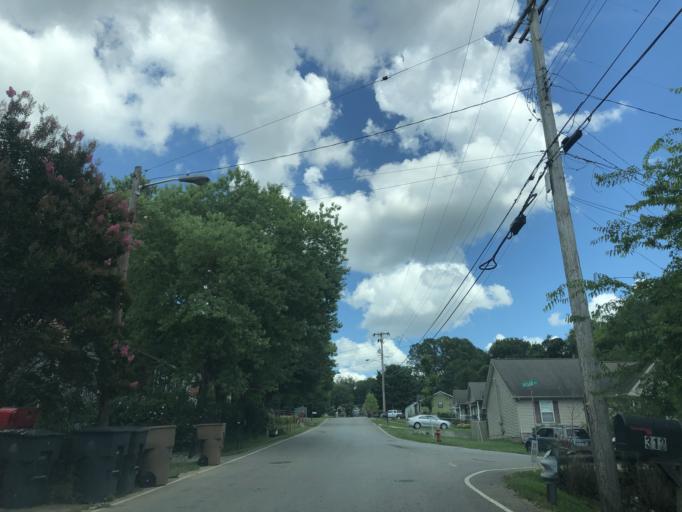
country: US
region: Tennessee
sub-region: Davidson County
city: Oak Hill
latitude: 36.0750
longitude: -86.7206
